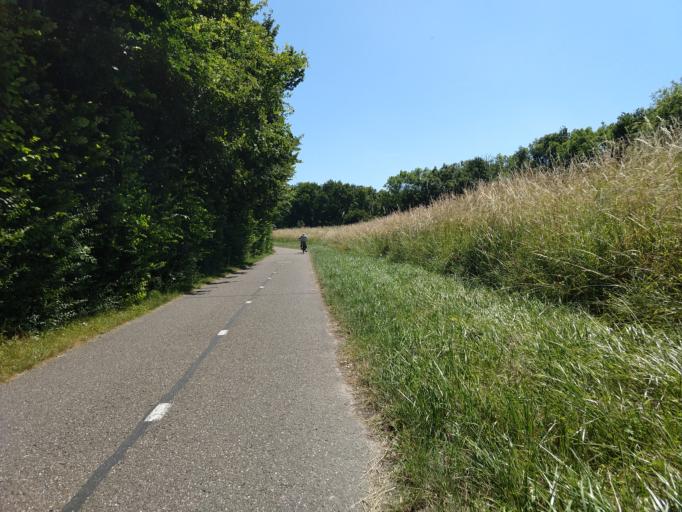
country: NL
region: Zeeland
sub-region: Gemeente Veere
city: Veere
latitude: 51.5601
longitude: 3.6430
